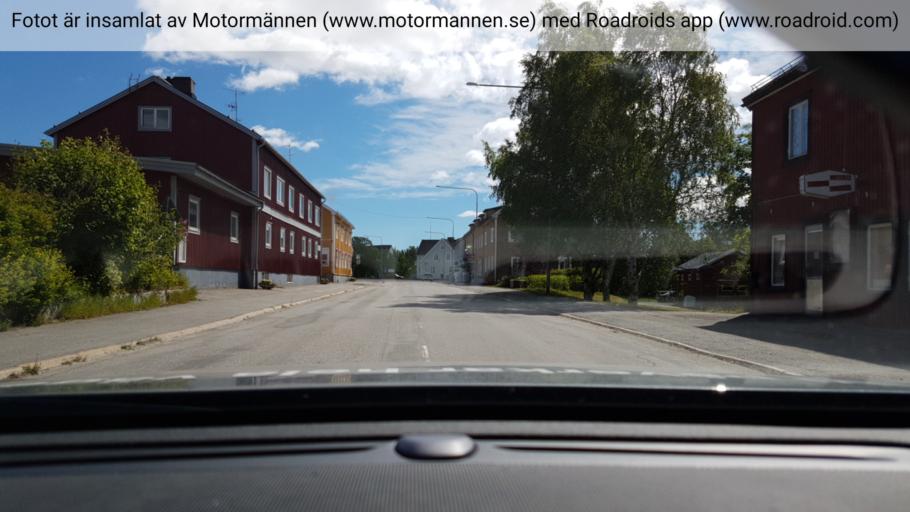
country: SE
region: Vaesterbotten
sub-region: Skelleftea Kommun
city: Burea
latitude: 64.3699
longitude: 21.3128
